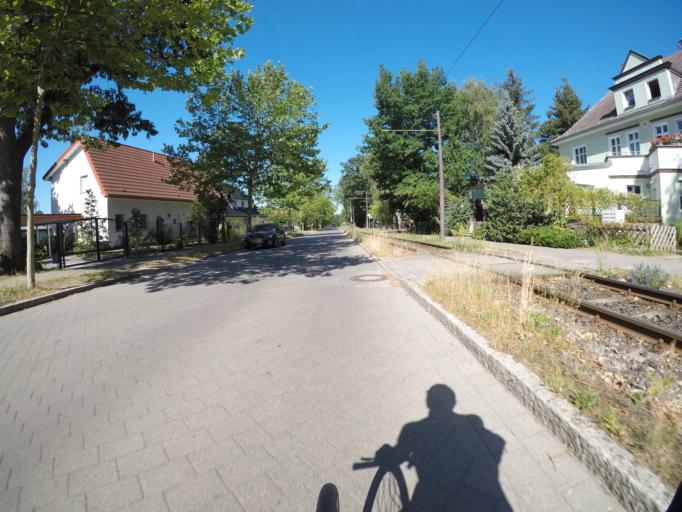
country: DE
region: Brandenburg
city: Woltersdorf
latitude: 52.4557
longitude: 13.7298
